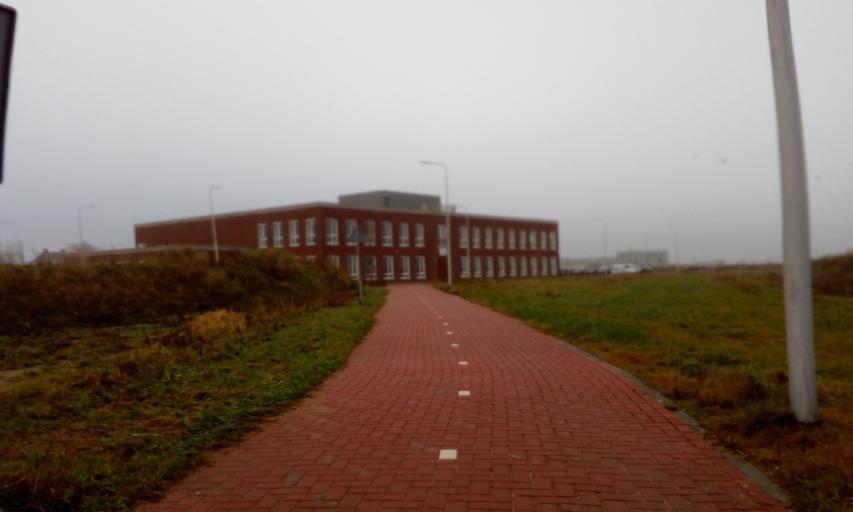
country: NL
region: South Holland
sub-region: Gemeente Lansingerland
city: Berkel en Rodenrijs
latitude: 51.9854
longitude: 4.4525
